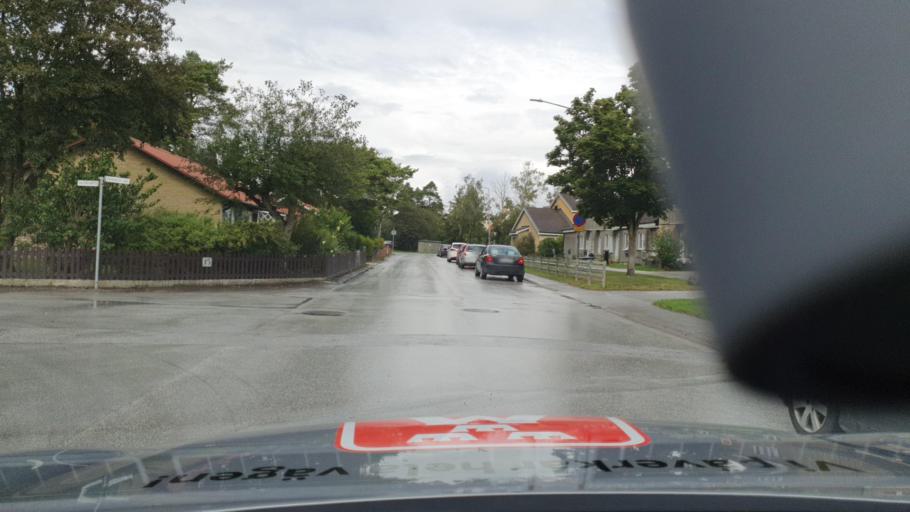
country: SE
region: Gotland
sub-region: Gotland
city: Slite
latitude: 57.7049
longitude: 18.8013
